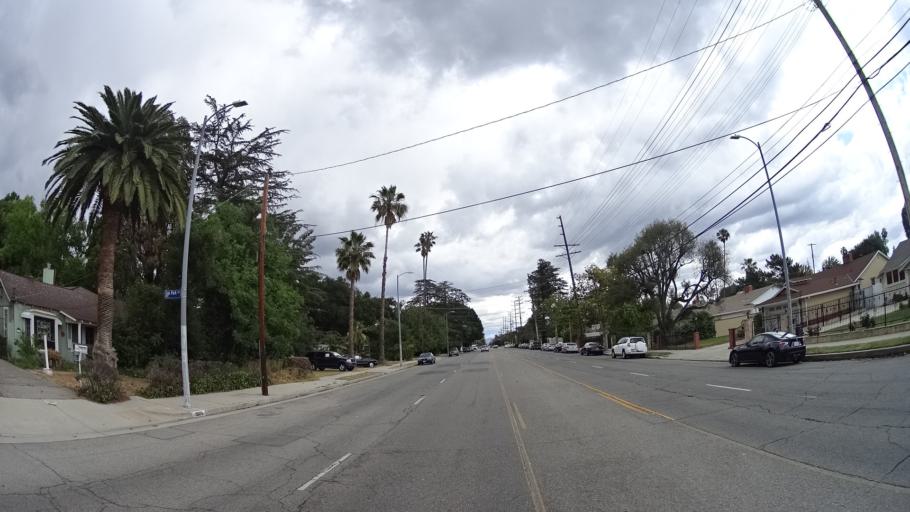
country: US
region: California
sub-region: Los Angeles County
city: Sherman Oaks
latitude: 34.1649
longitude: -118.4170
